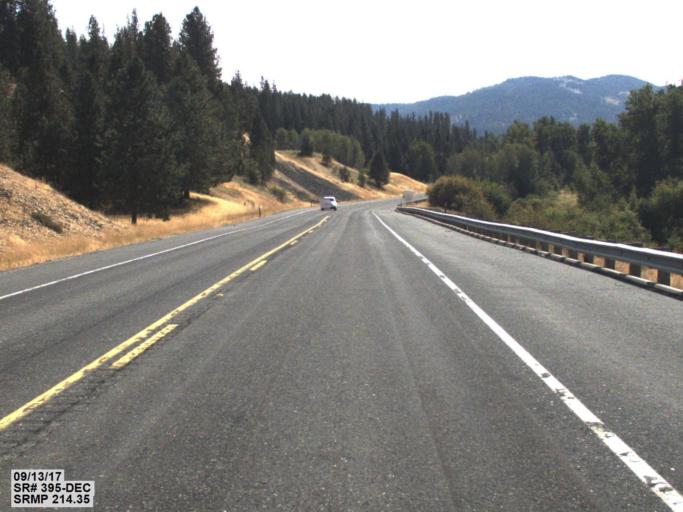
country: US
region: Washington
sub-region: Stevens County
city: Chewelah
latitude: 48.3363
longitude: -117.8293
